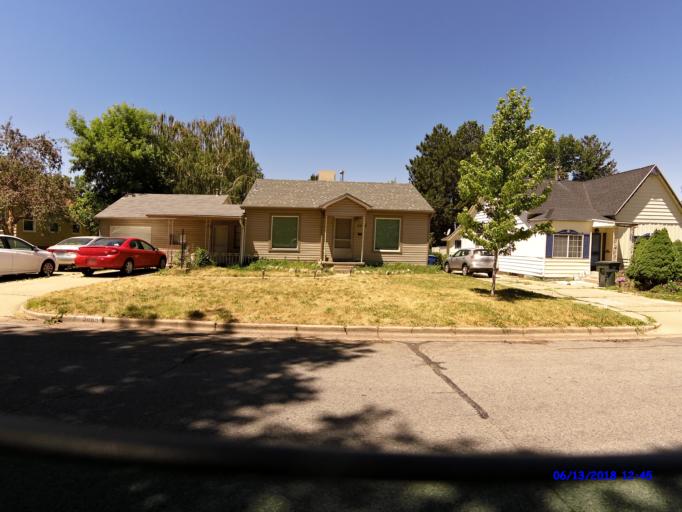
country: US
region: Utah
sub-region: Weber County
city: South Ogden
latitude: 41.2003
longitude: -111.9514
